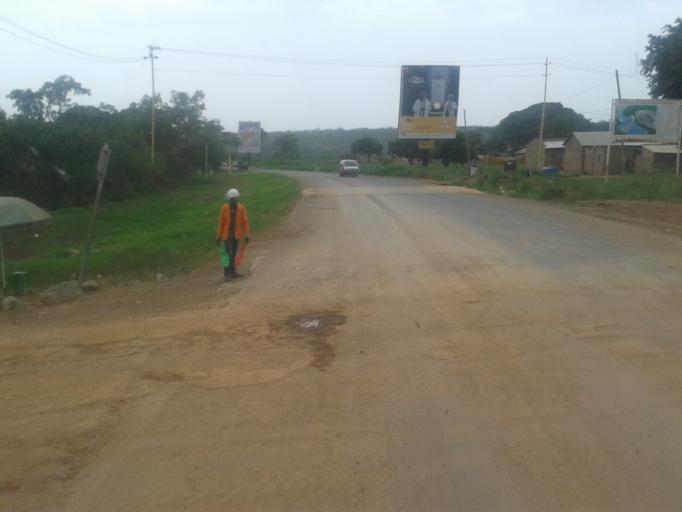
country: UG
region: Northern Region
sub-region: Oyam District
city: Oyam
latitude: 2.2356
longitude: 32.2463
